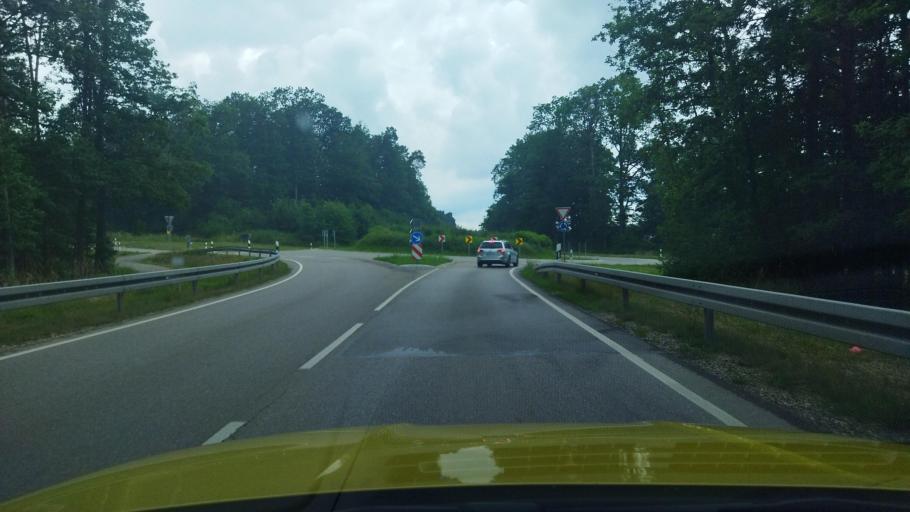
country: DE
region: Bavaria
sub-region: Regierungsbezirk Mittelfranken
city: Pfofeld
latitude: 49.1171
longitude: 10.8481
